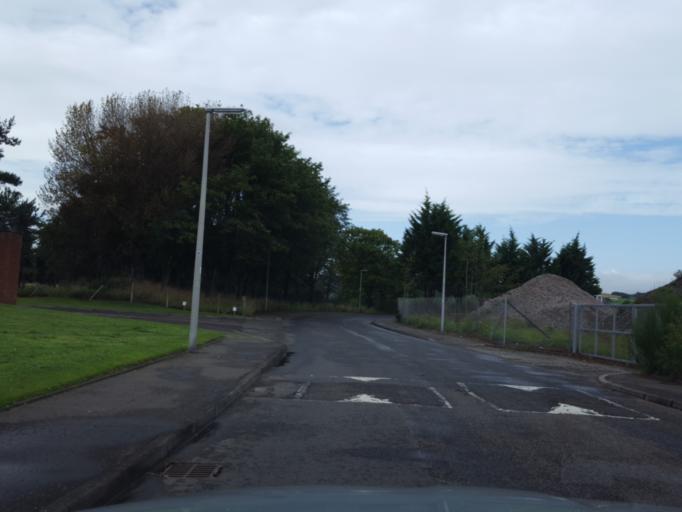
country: GB
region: Scotland
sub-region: Fife
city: Tayport
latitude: 56.4413
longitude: -2.8703
